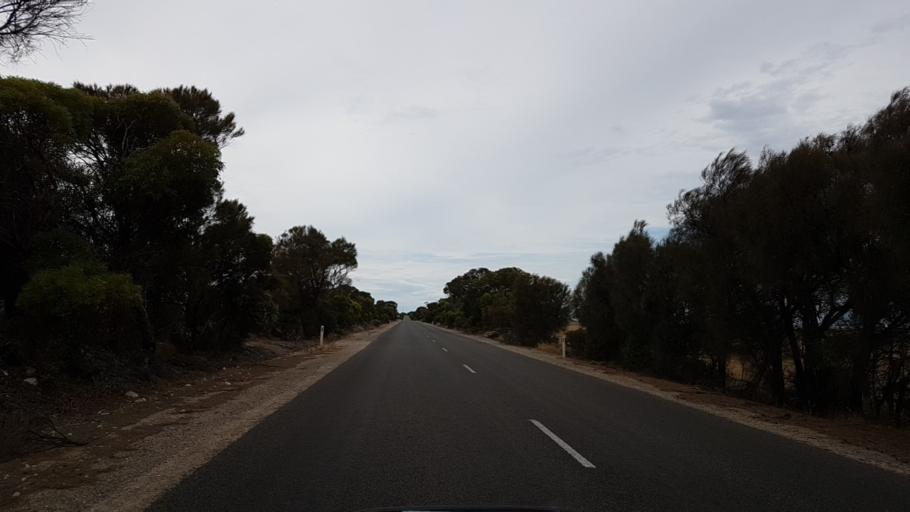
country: AU
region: South Australia
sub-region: Yorke Peninsula
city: Honiton
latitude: -34.9748
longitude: 137.1150
